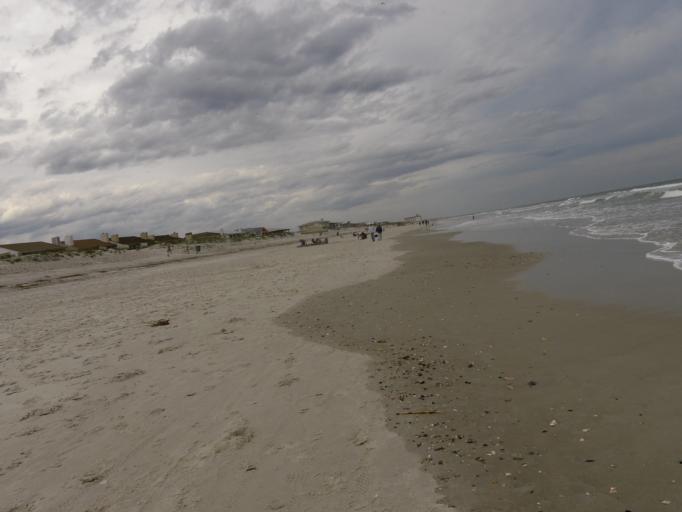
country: US
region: Florida
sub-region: Duval County
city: Neptune Beach
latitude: 30.3087
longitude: -81.3918
